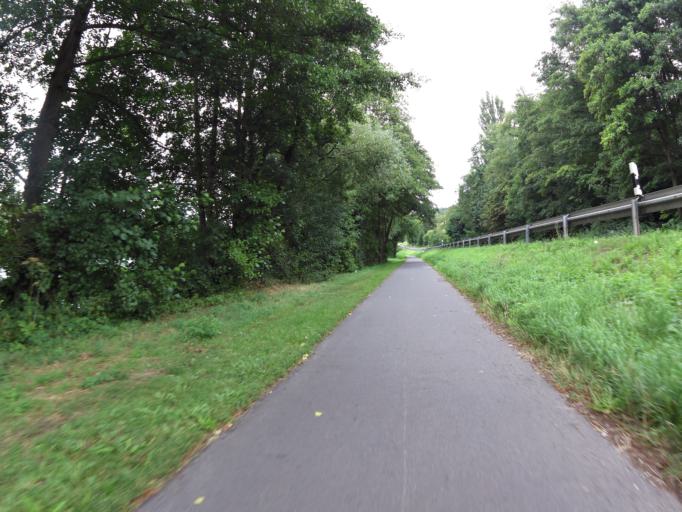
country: DE
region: Bavaria
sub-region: Regierungsbezirk Unterfranken
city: Eltmann
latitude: 49.9755
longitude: 10.6505
